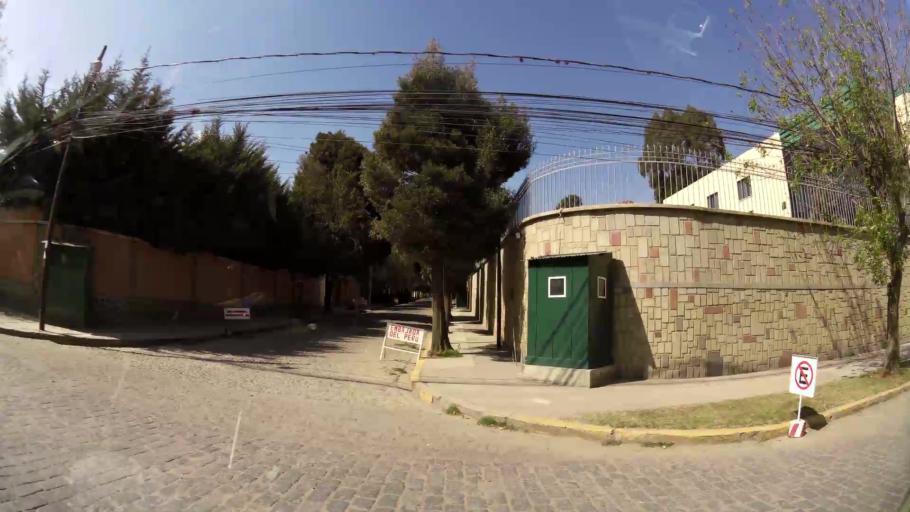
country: BO
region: La Paz
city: La Paz
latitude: -16.5443
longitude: -68.0917
